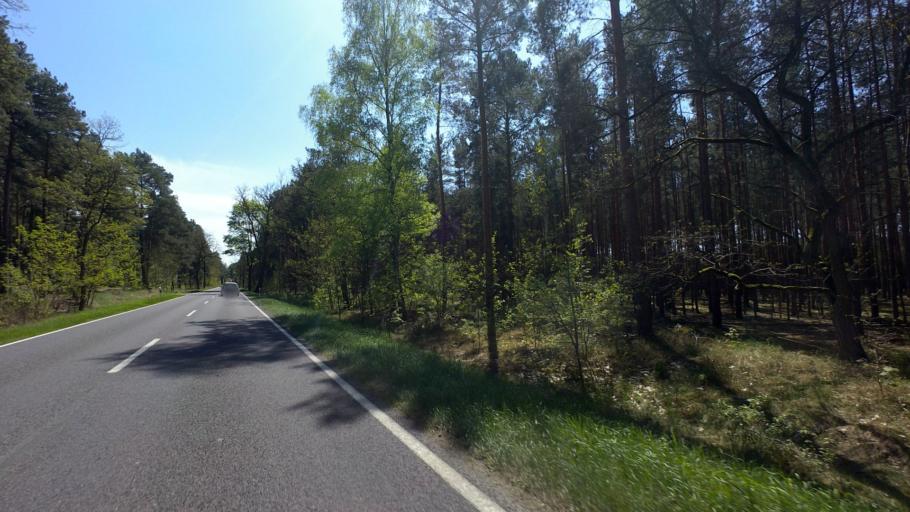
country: DE
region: Brandenburg
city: Gross Koris
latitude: 52.1796
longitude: 13.7116
